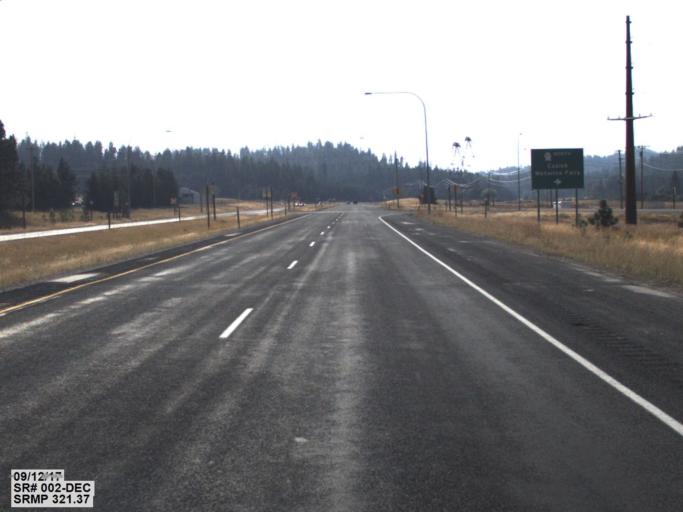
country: US
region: Washington
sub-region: Spokane County
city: Deer Park
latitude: 48.0973
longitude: -117.2768
